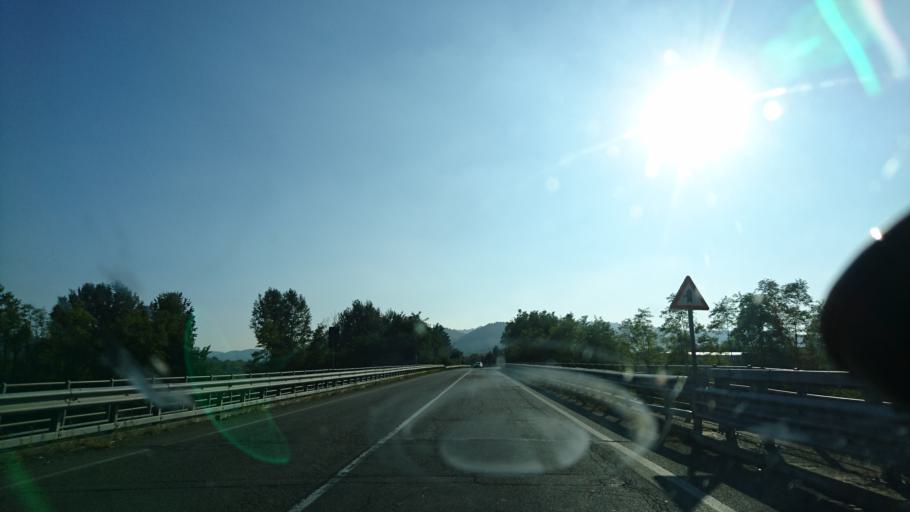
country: IT
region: Piedmont
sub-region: Provincia di Alessandria
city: Terzo
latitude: 44.6671
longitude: 8.4224
